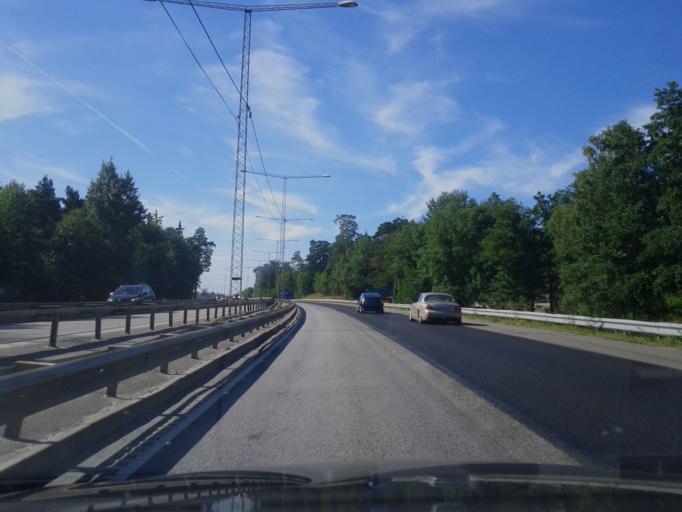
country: SE
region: Stockholm
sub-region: Danderyds Kommun
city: Djursholm
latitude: 59.4180
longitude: 18.0404
